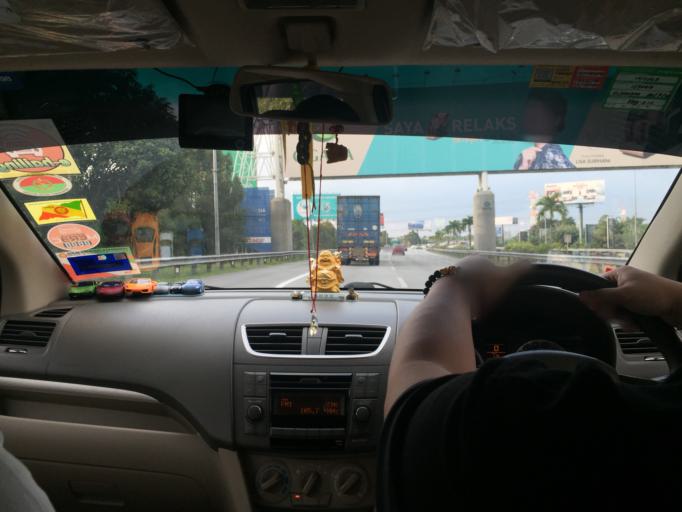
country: MY
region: Putrajaya
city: Putrajaya
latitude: 2.8177
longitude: 101.6630
